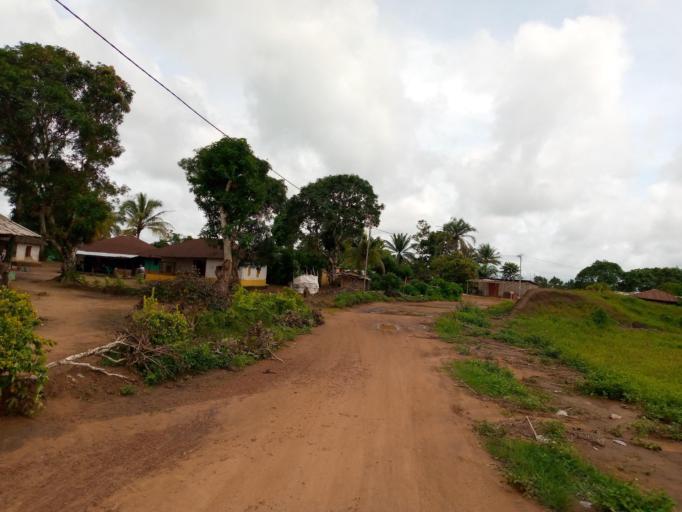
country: SL
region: Southern Province
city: Mogbwemo
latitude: 7.7644
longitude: -12.3108
